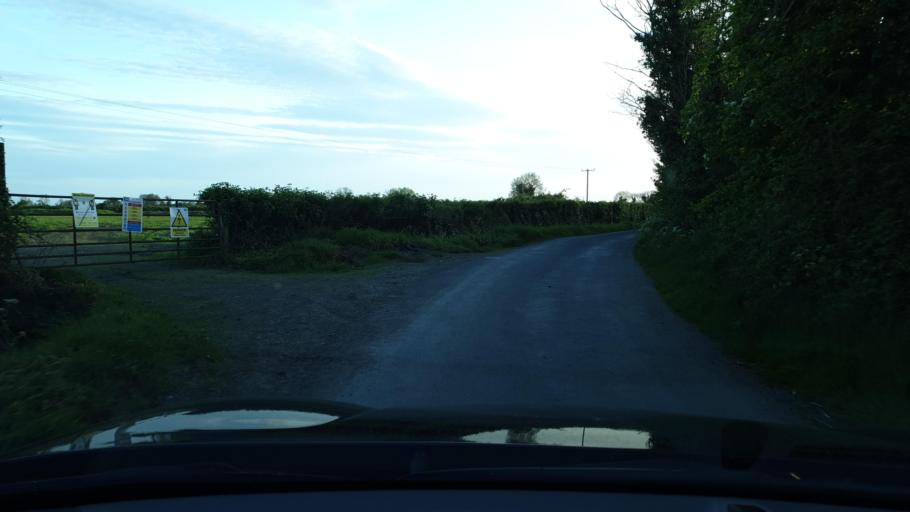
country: IE
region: Leinster
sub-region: An Mhi
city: Ashbourne
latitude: 53.4787
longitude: -6.3852
